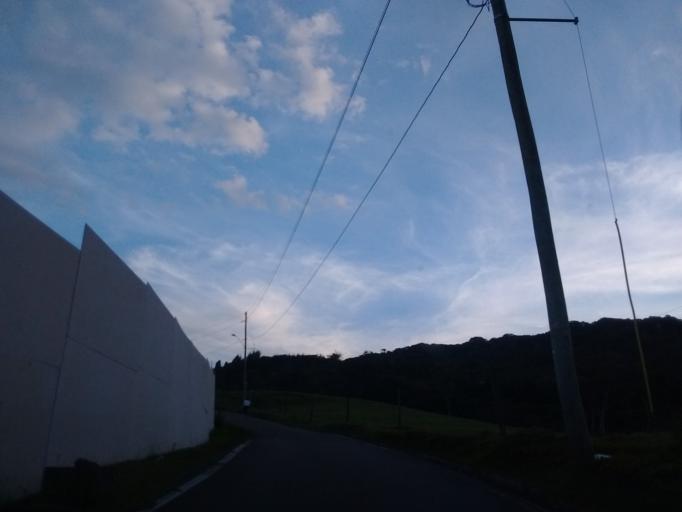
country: CO
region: Antioquia
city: Envigado
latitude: 6.1750
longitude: -75.5027
